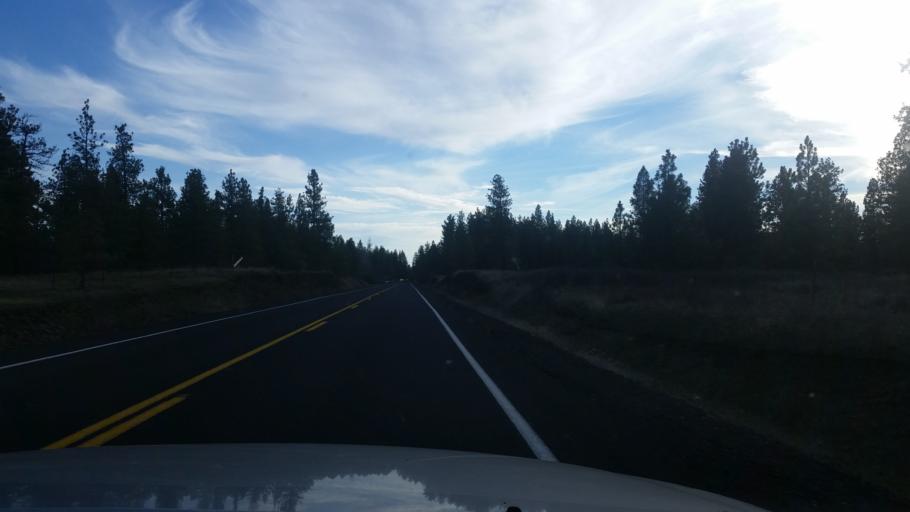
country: US
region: Washington
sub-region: Spokane County
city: Cheney
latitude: 47.4075
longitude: -117.5699
